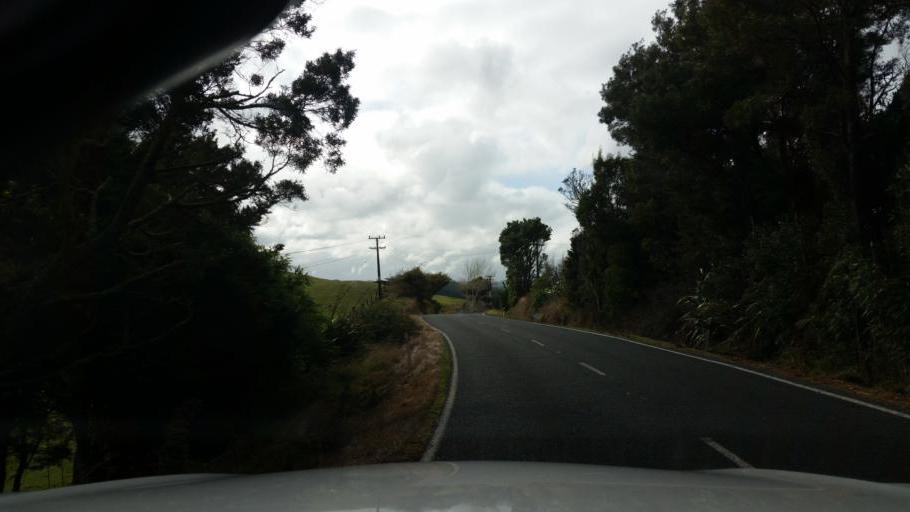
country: NZ
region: Northland
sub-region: Whangarei
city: Ruakaka
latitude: -36.0685
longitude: 174.2656
